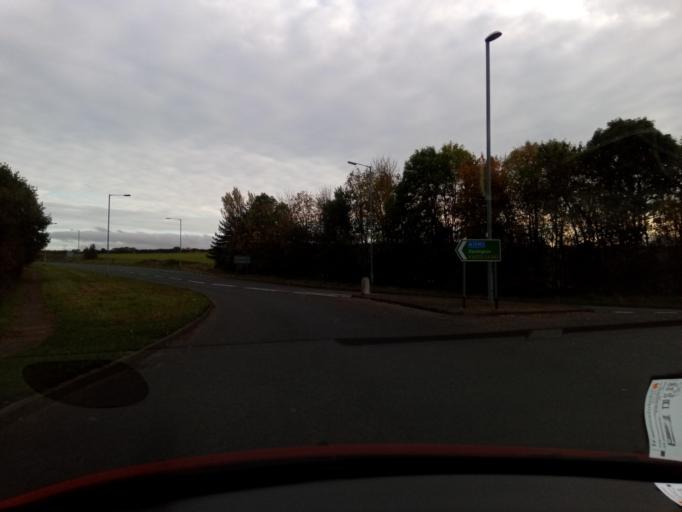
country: GB
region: England
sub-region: County Durham
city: Shildon
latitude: 54.6232
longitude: -1.6491
